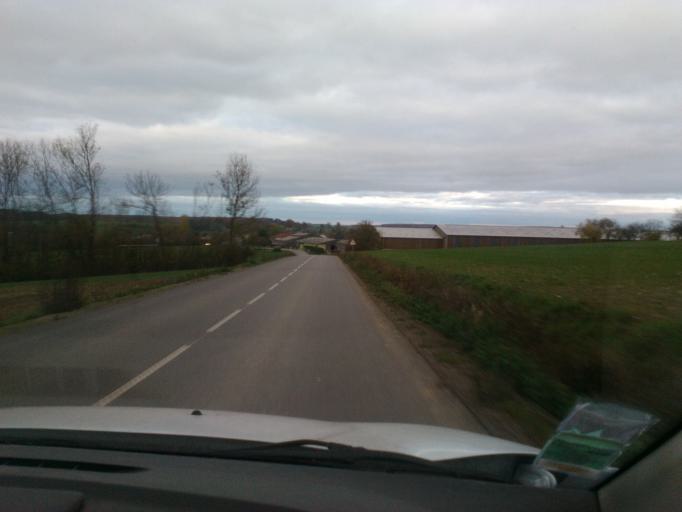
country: FR
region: Lorraine
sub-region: Departement des Vosges
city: Darnieulles
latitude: 48.2372
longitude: 6.3304
